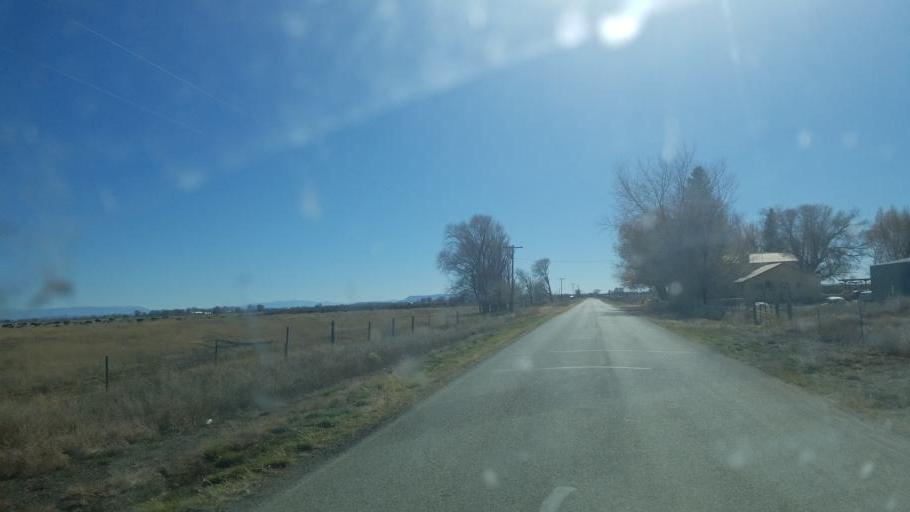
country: US
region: Colorado
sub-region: Alamosa County
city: Alamosa
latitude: 37.5308
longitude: -105.8944
